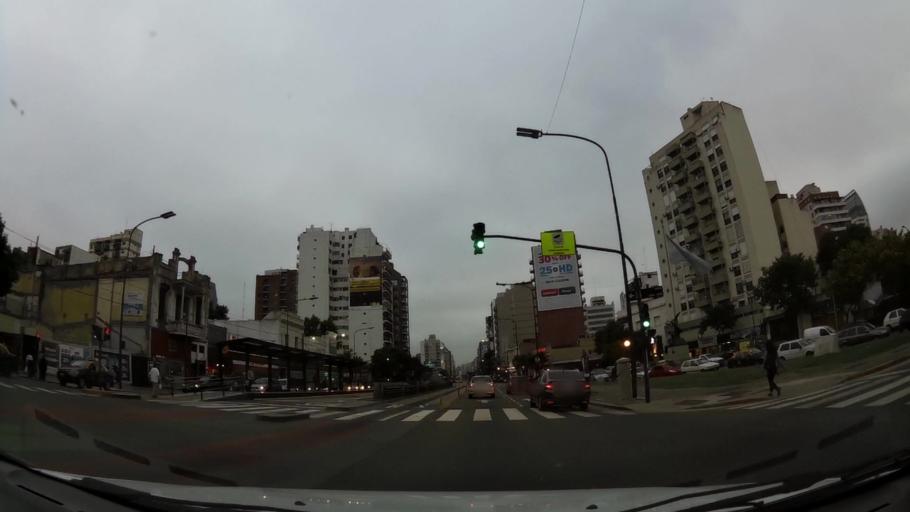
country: AR
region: Buenos Aires F.D.
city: Colegiales
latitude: -34.5461
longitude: -58.4705
